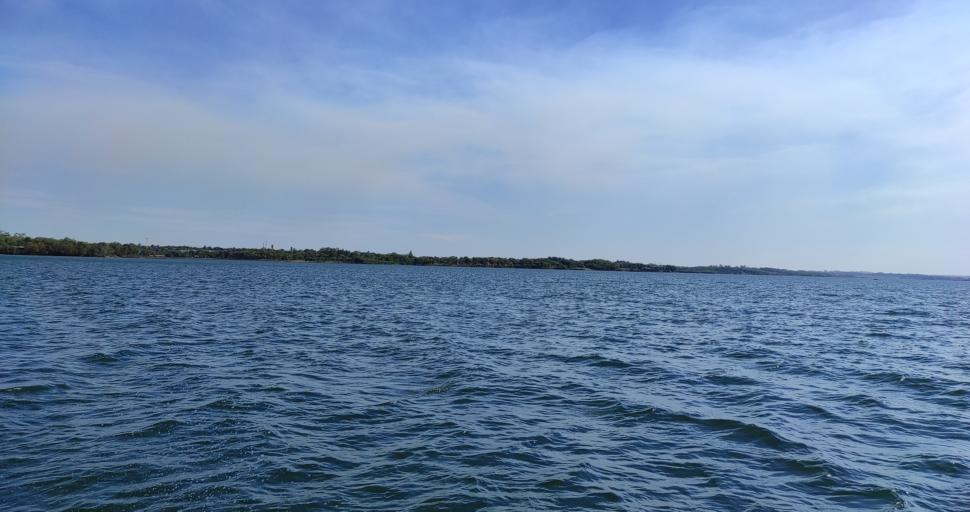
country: PY
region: Itapua
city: San Juan del Parana
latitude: -27.3440
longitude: -55.9438
